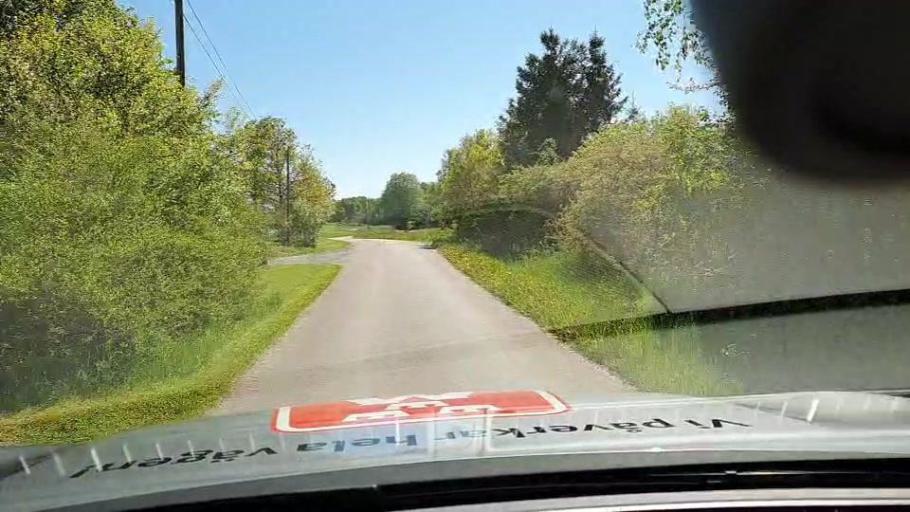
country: SE
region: Soedermanland
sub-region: Strangnas Kommun
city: Strangnas
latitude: 59.4591
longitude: 16.8819
